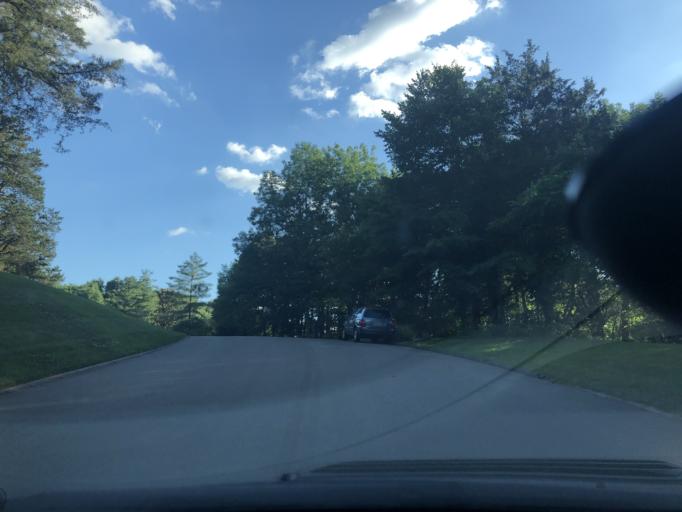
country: US
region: Tennessee
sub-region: Davidson County
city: Forest Hills
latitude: 36.0602
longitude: -86.8329
